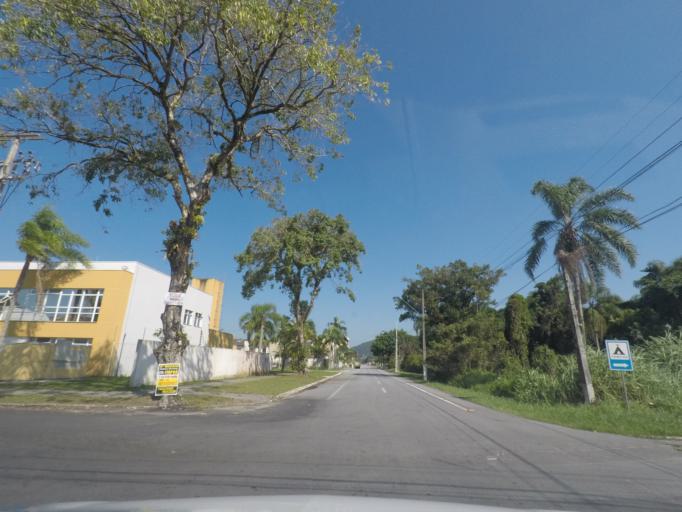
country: BR
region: Parana
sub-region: Guaratuba
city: Guaratuba
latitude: -25.8255
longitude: -48.5368
